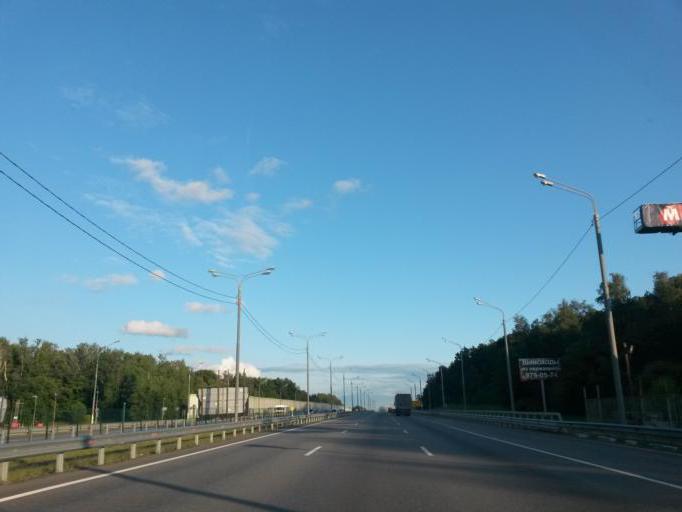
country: RU
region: Moskovskaya
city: Yam
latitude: 55.4712
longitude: 37.7516
